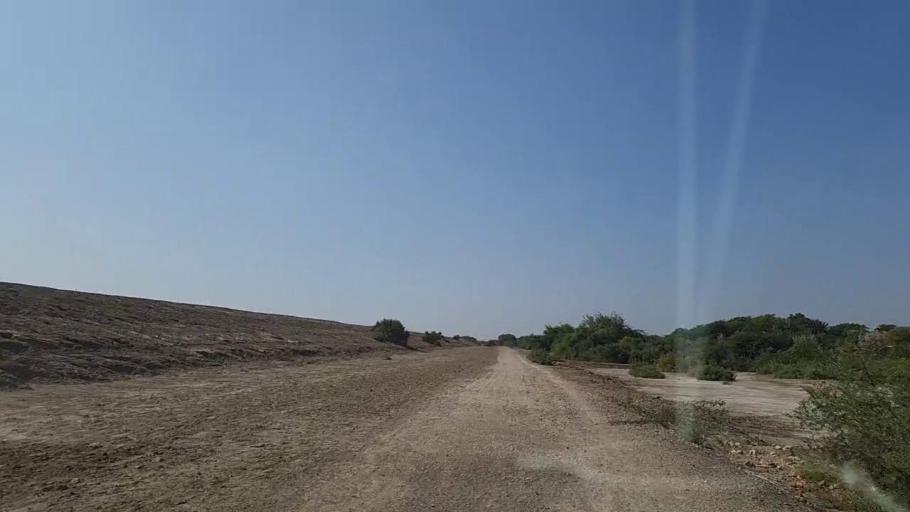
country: PK
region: Sindh
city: Chuhar Jamali
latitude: 24.4889
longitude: 68.0144
